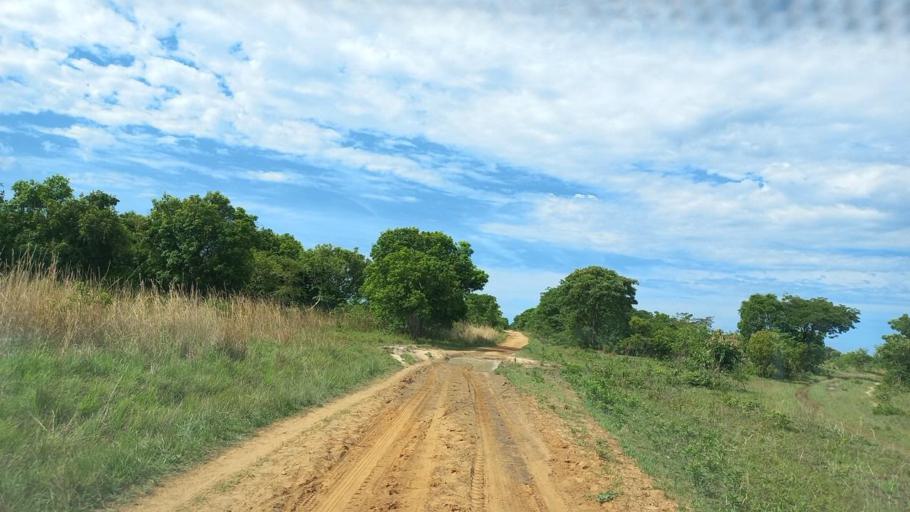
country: ZM
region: North-Western
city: Kabompo
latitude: -13.5164
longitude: 24.3885
